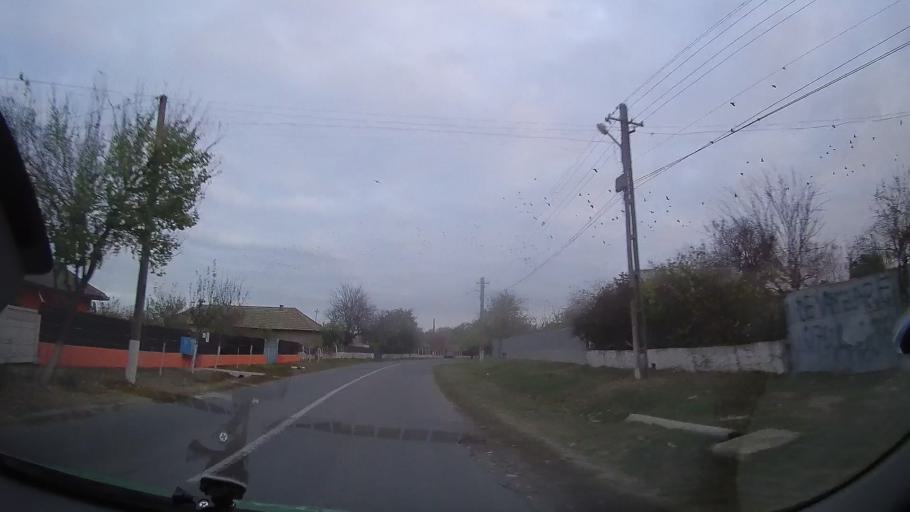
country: RO
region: Tulcea
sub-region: Comuna Mihai Bravu
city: Turda
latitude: 44.9723
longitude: 28.6266
